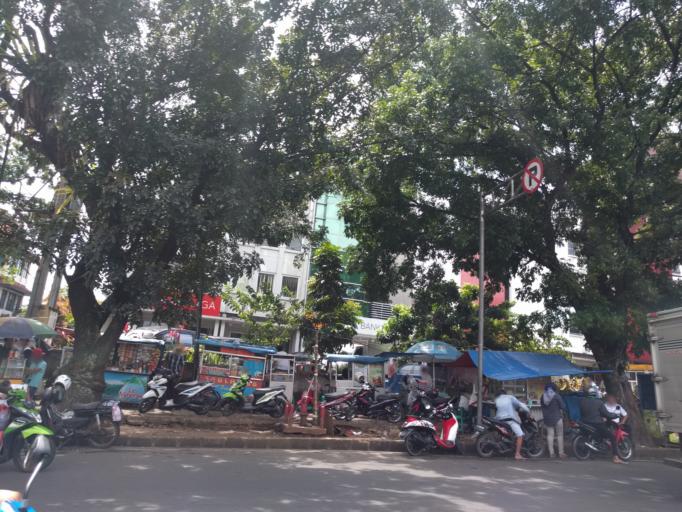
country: ID
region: West Java
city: Bogor
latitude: -6.6211
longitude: 106.8165
